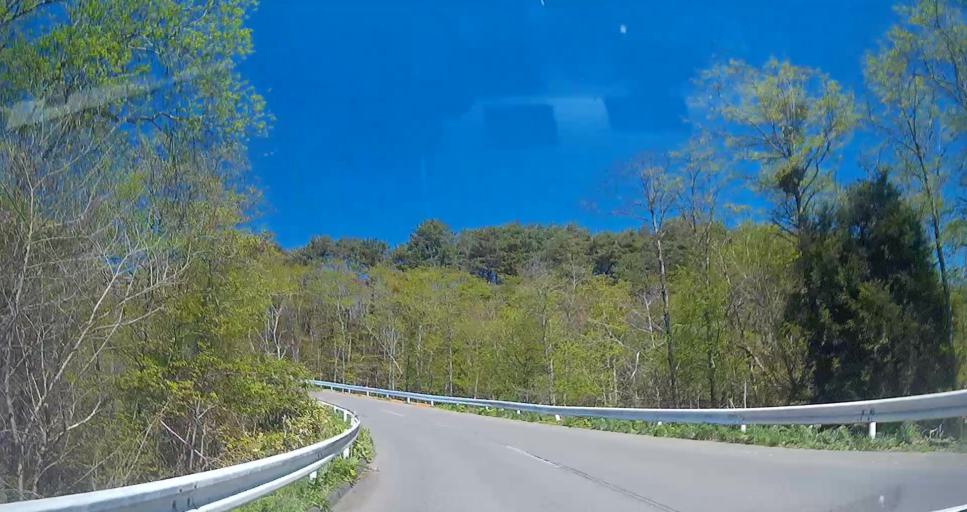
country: JP
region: Aomori
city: Mutsu
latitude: 41.2591
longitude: 141.3914
